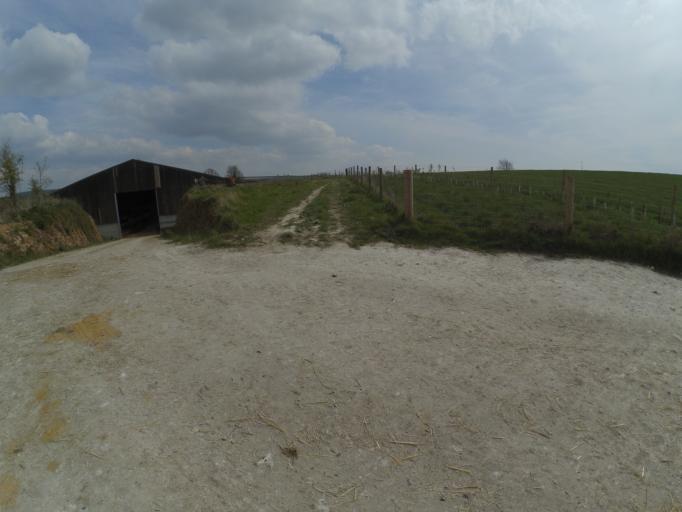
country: GB
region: England
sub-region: West Sussex
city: Arundel
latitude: 50.8800
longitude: -0.5459
